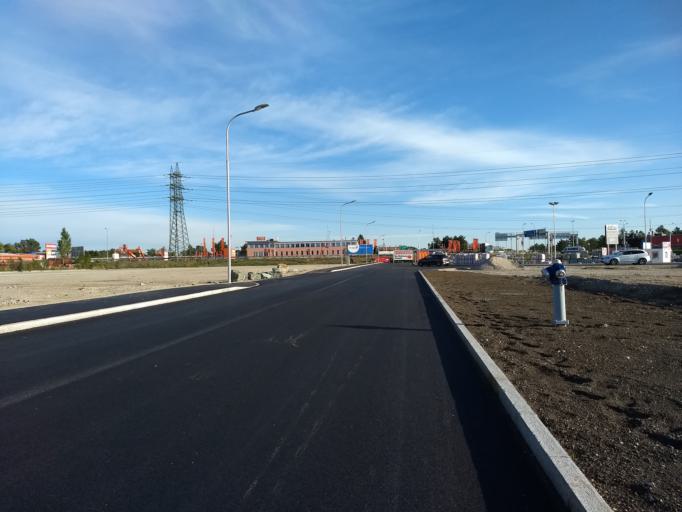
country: AT
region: Lower Austria
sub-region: Politischer Bezirk Modling
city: Wiener Neudorf
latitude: 48.0771
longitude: 16.3291
